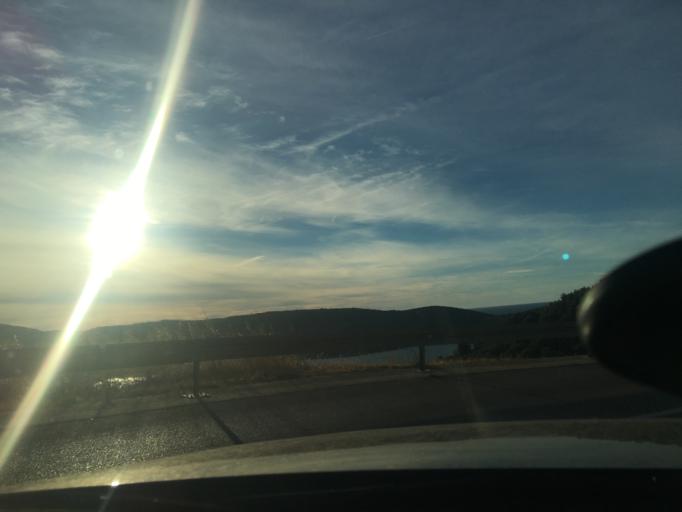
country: HR
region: Splitsko-Dalmatinska
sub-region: Grad Vis
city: Vis
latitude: 43.0564
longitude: 16.2050
